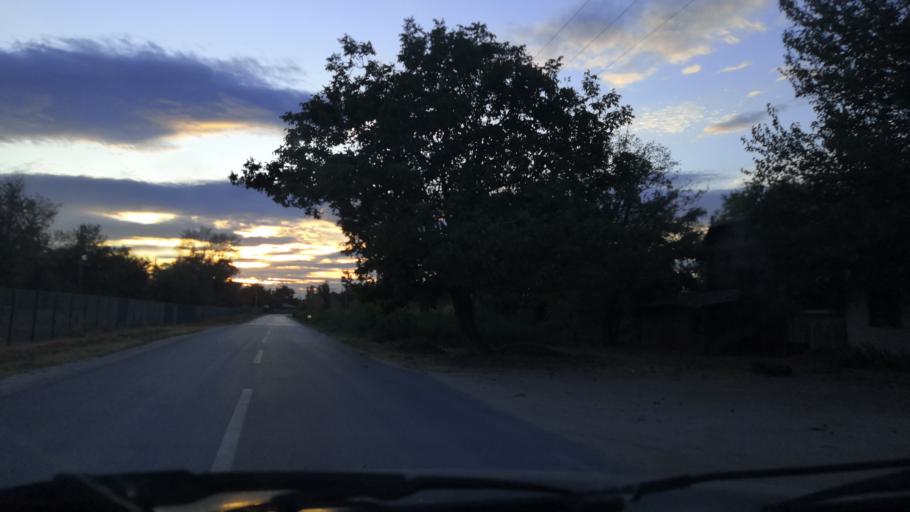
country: RO
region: Mehedinti
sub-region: Comuna Gogosu
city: Balta Verde
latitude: 44.2906
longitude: 22.6056
